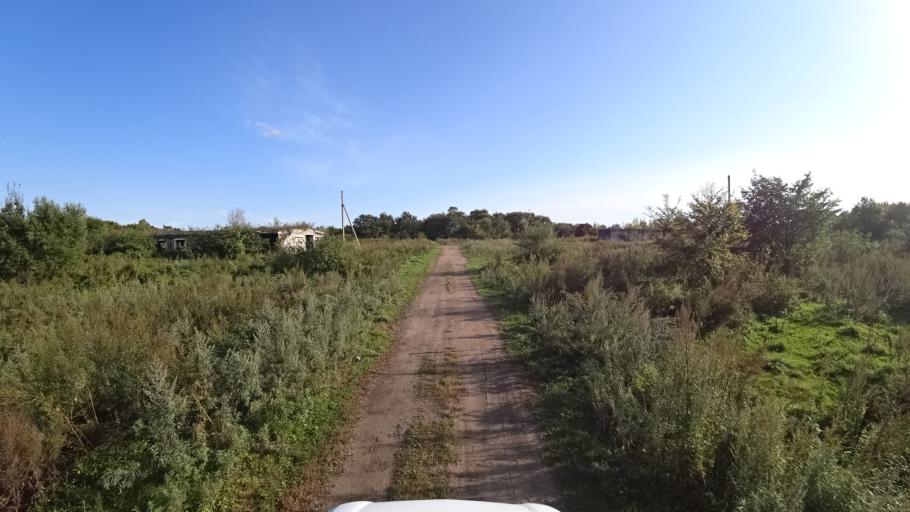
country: RU
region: Amur
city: Arkhara
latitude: 49.3480
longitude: 130.1068
